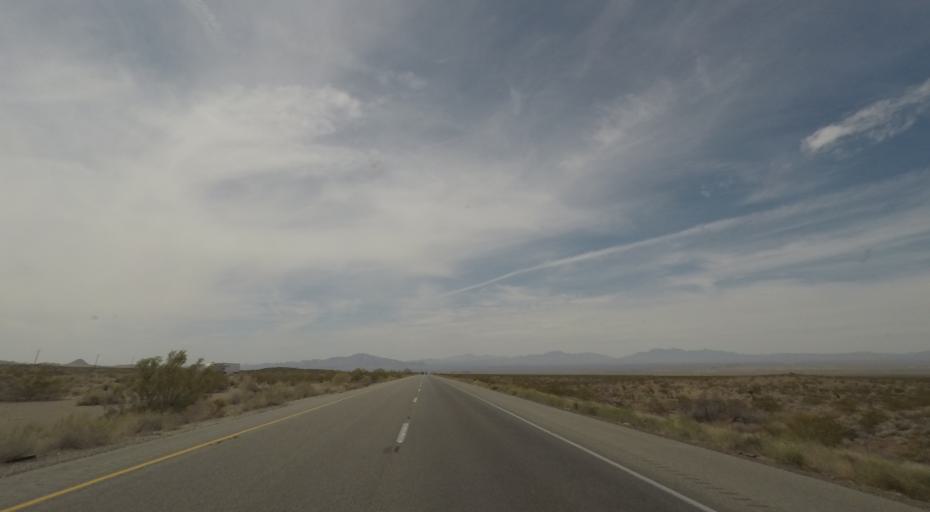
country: US
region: California
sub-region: San Bernardino County
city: Needles
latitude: 34.8280
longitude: -115.0655
